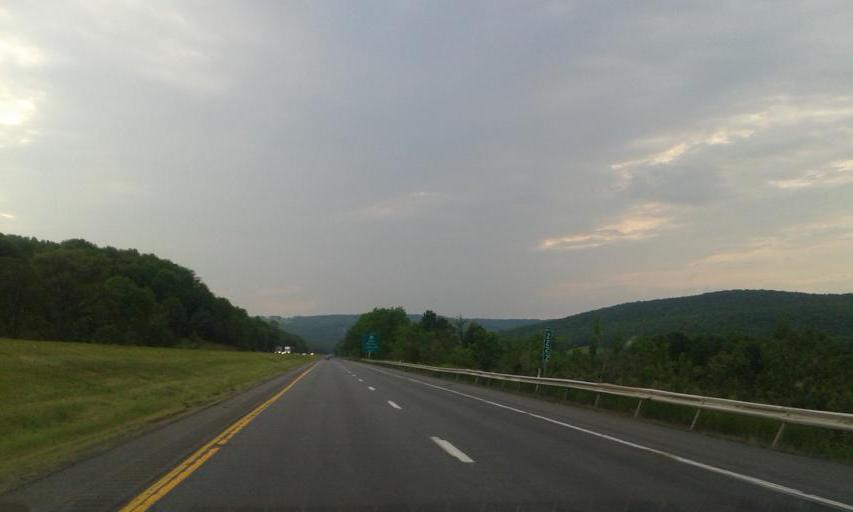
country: US
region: Pennsylvania
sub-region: Susquehanna County
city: Hallstead
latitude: 41.8610
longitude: -75.6925
